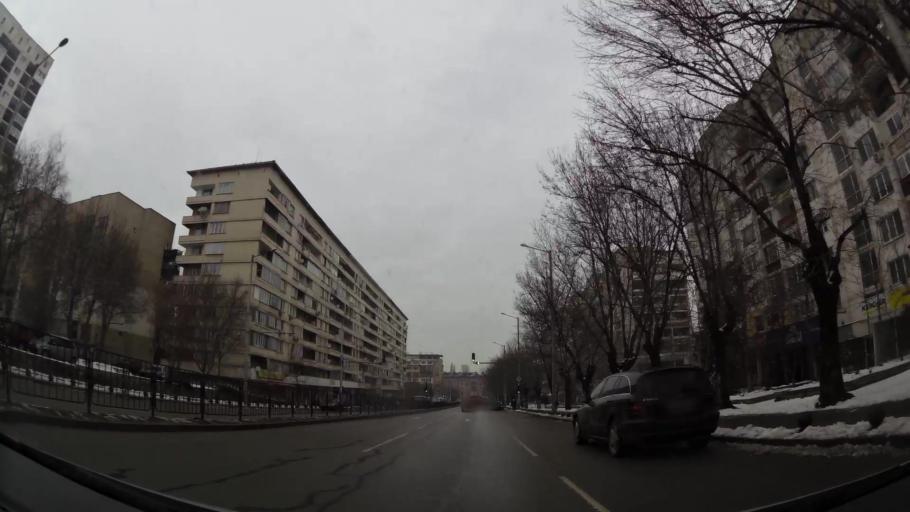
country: BG
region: Sofia-Capital
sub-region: Stolichna Obshtina
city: Sofia
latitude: 42.7109
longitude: 23.3143
